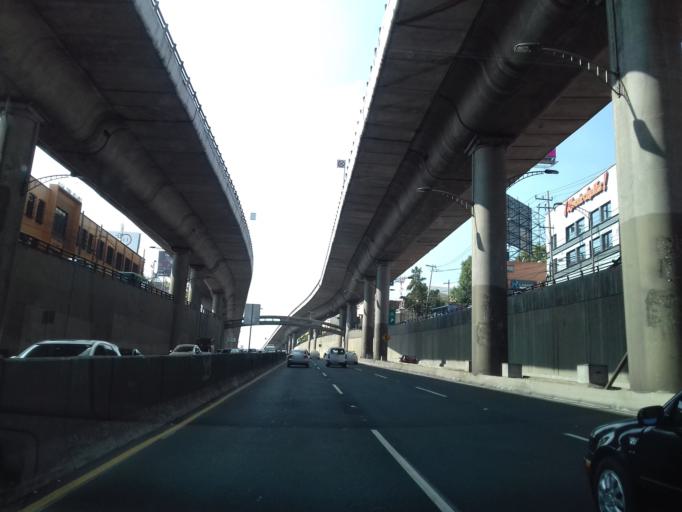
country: MX
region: Mexico City
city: Alvaro Obregon
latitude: 19.3463
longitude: -99.2023
